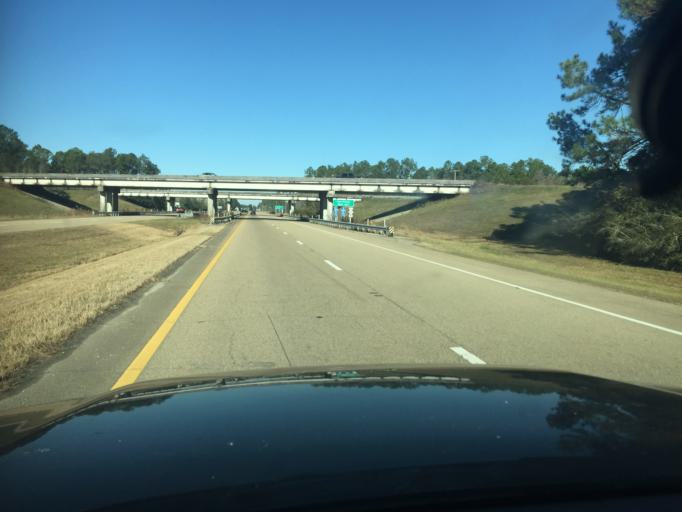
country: US
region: Mississippi
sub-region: Hancock County
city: Pearlington
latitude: 30.3149
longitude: -89.5968
